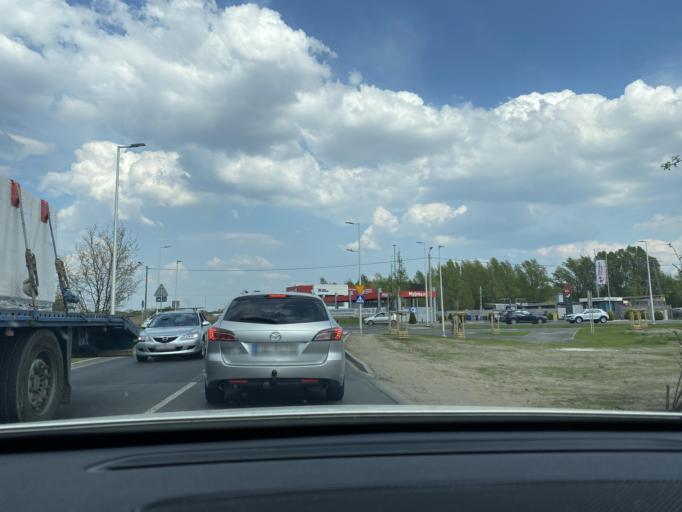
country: PL
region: Lower Silesian Voivodeship
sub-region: Powiat wroclawski
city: Wilczyce
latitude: 51.1217
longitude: 17.1196
